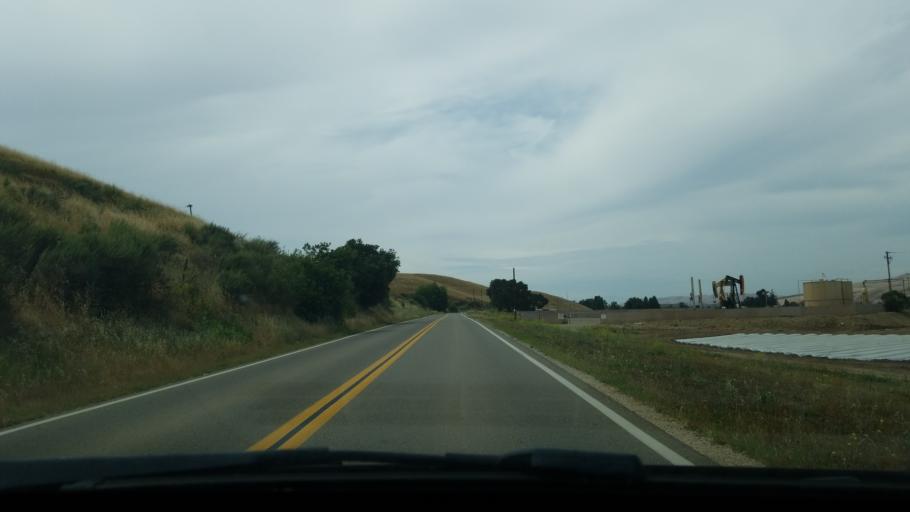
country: US
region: California
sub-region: Santa Barbara County
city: Orcutt
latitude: 34.8745
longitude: -120.3087
